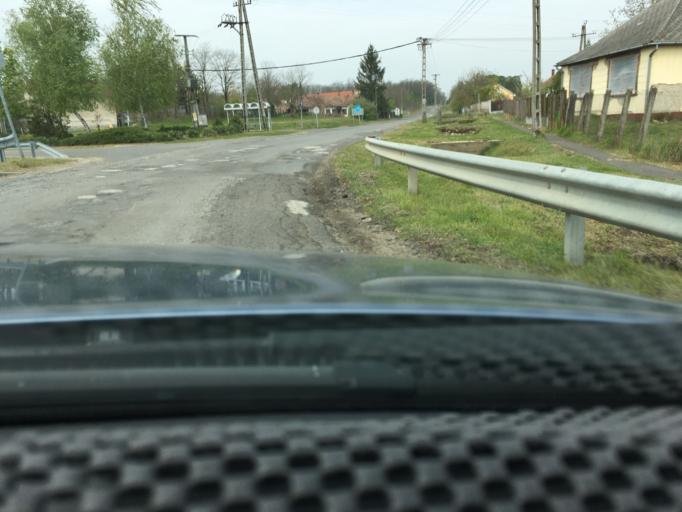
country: HU
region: Szabolcs-Szatmar-Bereg
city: Nyirlugos
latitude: 47.6908
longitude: 22.0345
